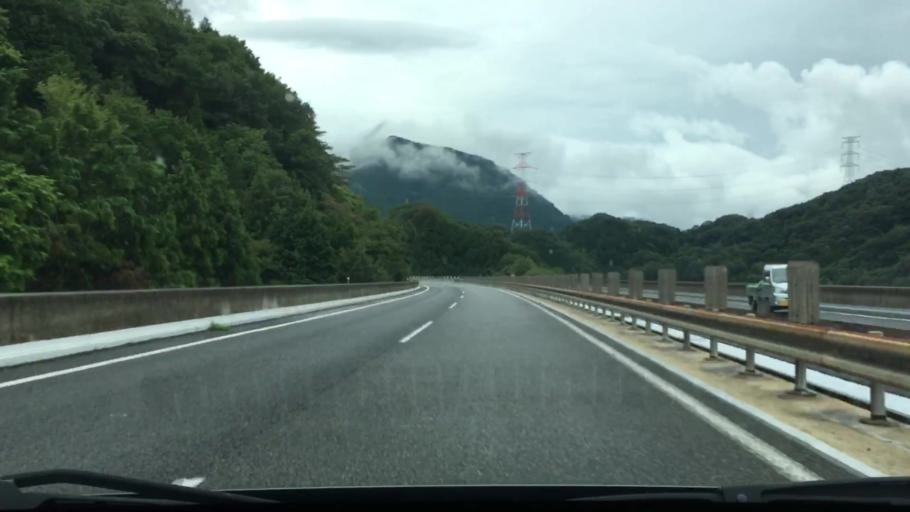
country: JP
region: Hiroshima
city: Hiroshima-shi
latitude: 34.5618
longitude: 132.4519
